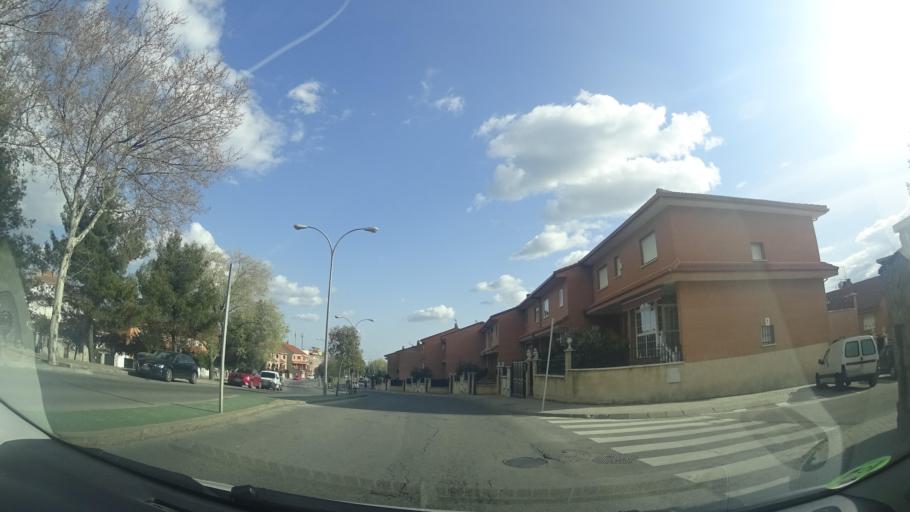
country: ES
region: Madrid
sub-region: Provincia de Madrid
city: Colmenar Viejo
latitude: 40.6570
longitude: -3.7762
